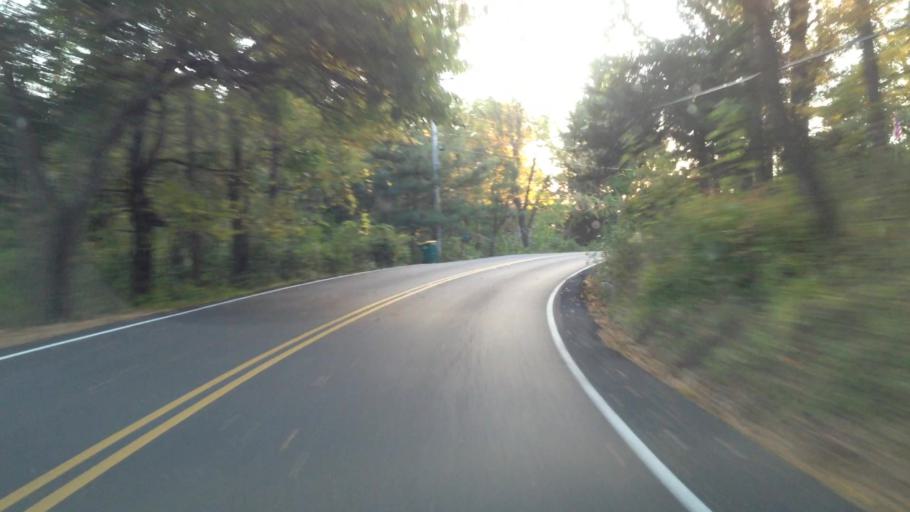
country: US
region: New York
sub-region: Ulster County
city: Tillson
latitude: 41.8245
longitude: -74.0074
